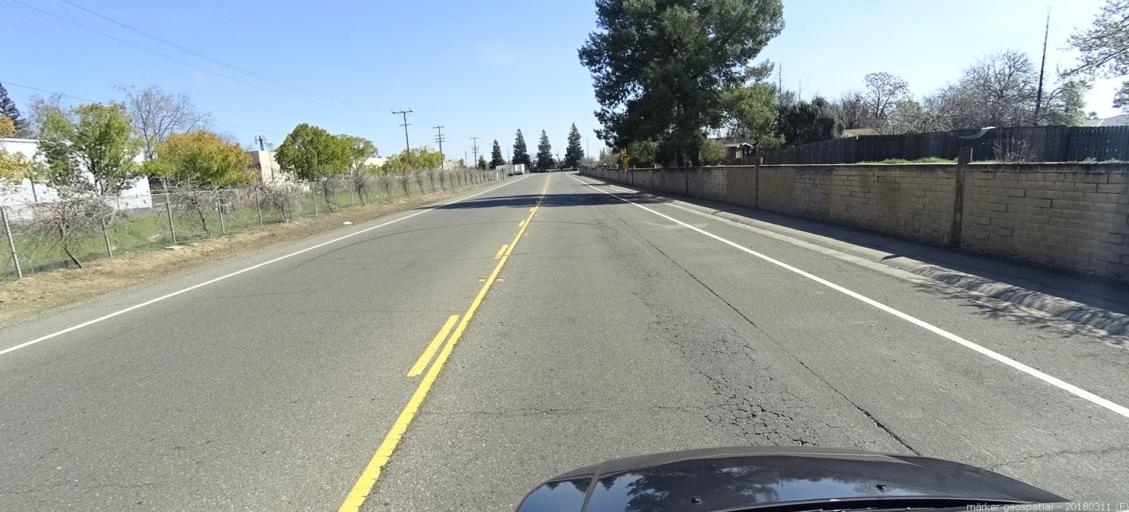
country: US
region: California
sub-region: Sacramento County
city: Florin
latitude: 38.4742
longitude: -121.3929
